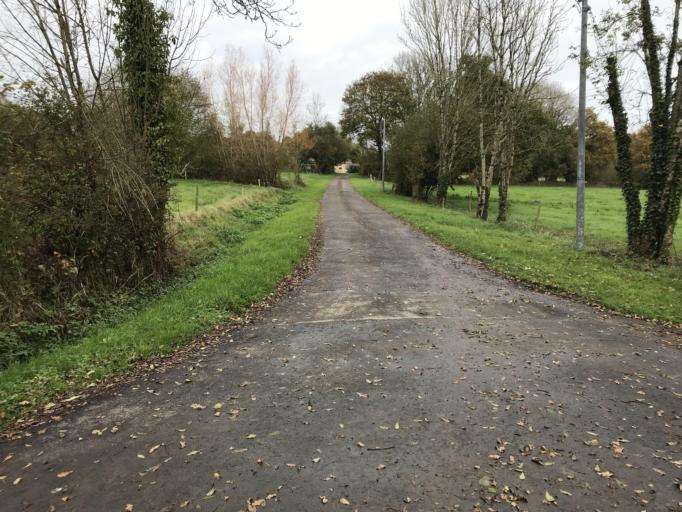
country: FR
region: Brittany
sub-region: Departement du Finistere
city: Irvillac
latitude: 48.3477
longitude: -4.2147
